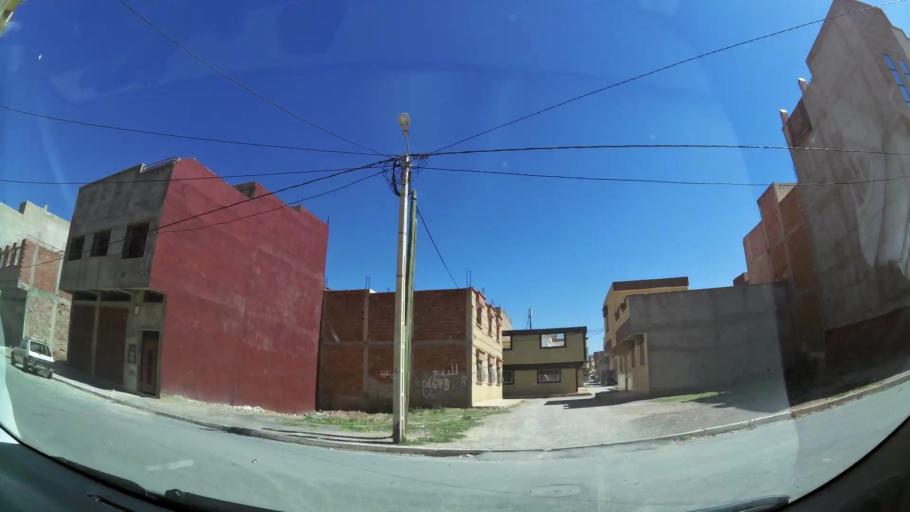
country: MA
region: Oriental
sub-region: Oujda-Angad
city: Oujda
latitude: 34.6593
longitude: -1.8748
